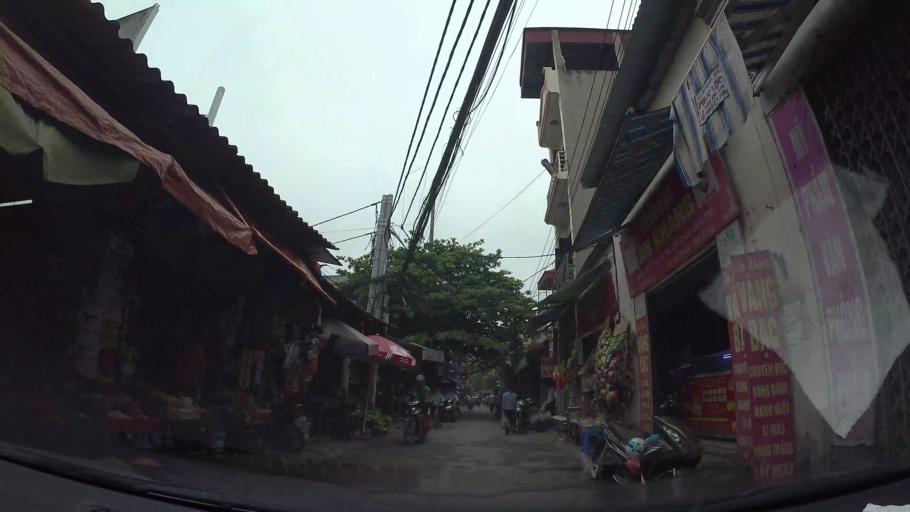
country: VN
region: Ha Noi
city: Hai BaTrung
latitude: 20.9865
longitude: 105.8885
